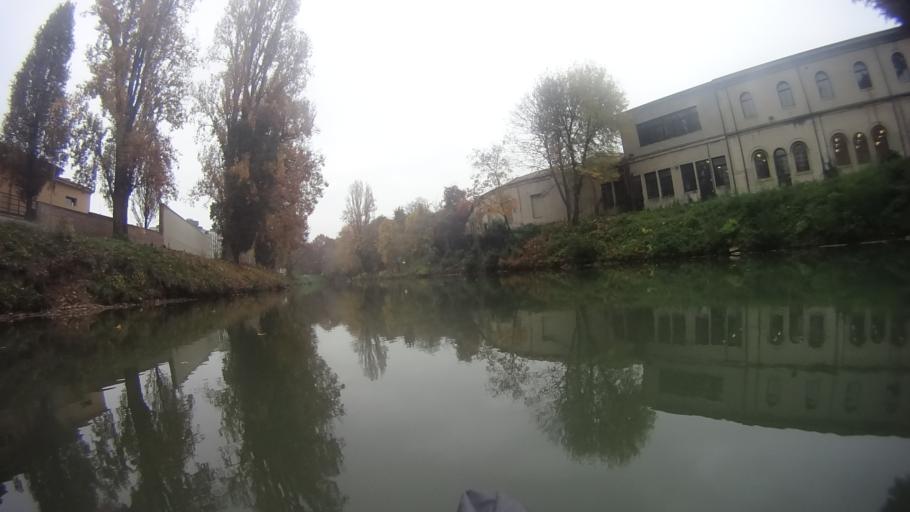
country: IT
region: Veneto
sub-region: Provincia di Padova
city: Padova
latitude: 45.4113
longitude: 11.8828
